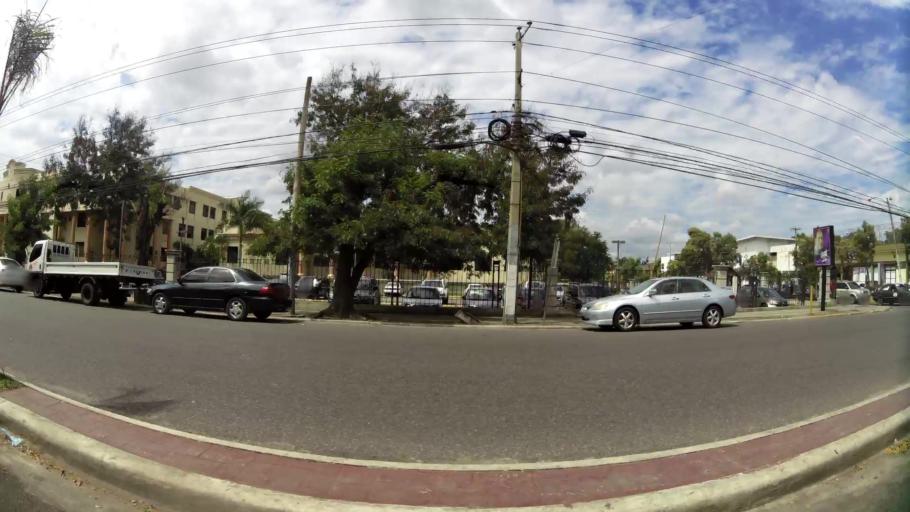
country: DO
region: Santiago
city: Santiago de los Caballeros
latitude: 19.4679
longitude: -70.7123
